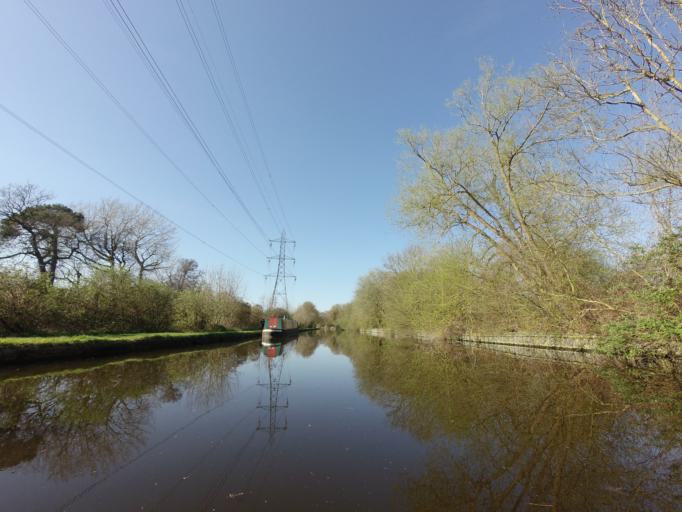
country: GB
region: England
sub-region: Buckinghamshire
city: Denham
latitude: 51.5695
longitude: -0.4816
